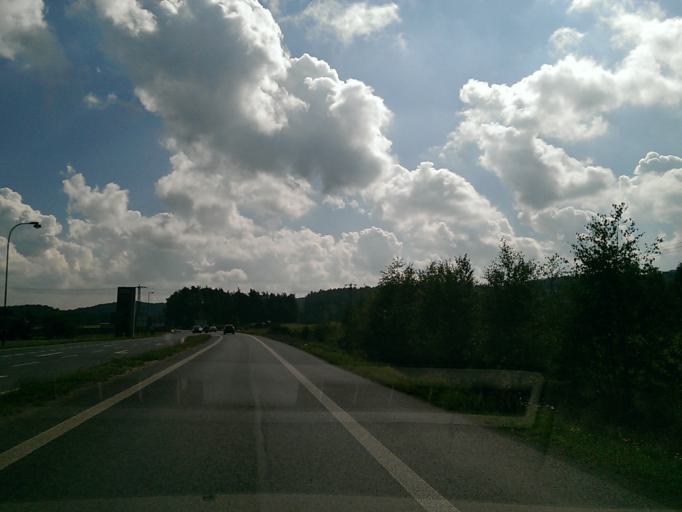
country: CZ
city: Duba
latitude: 50.6077
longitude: 14.5818
